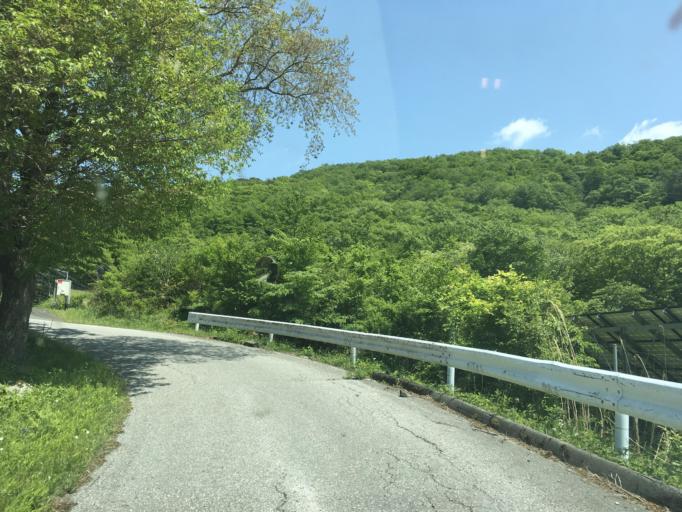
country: JP
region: Iwate
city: Ofunato
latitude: 39.1729
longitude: 141.7300
